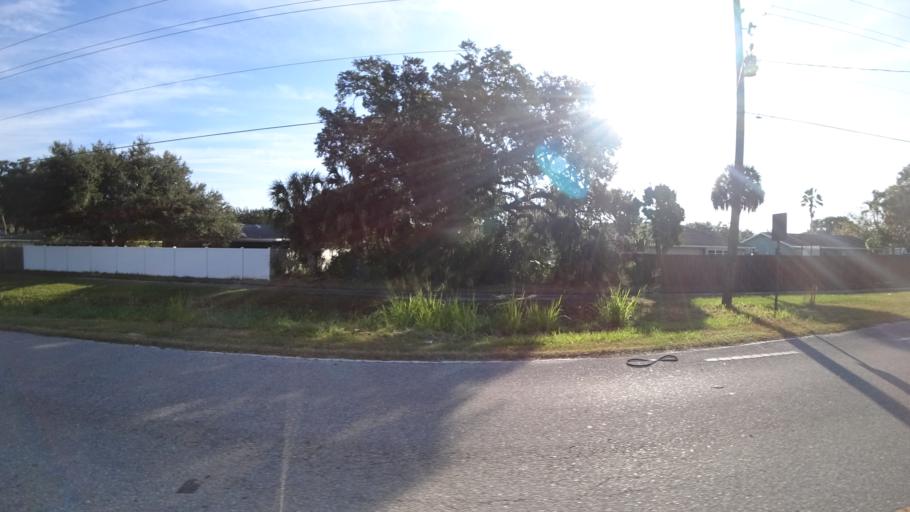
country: US
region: Florida
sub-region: Manatee County
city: Samoset
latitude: 27.4680
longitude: -82.5302
